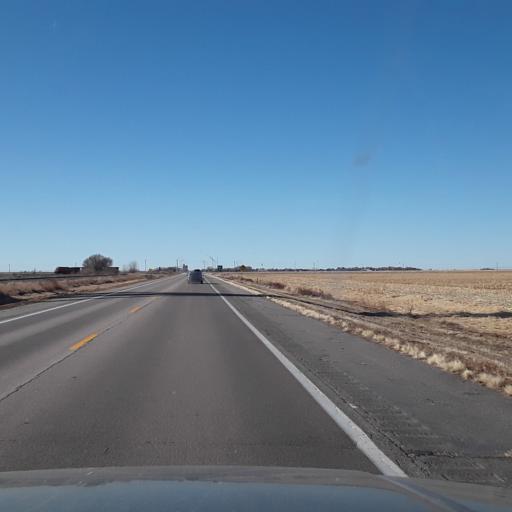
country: US
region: Nebraska
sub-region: Kearney County
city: Minden
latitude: 40.4852
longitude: -99.0765
